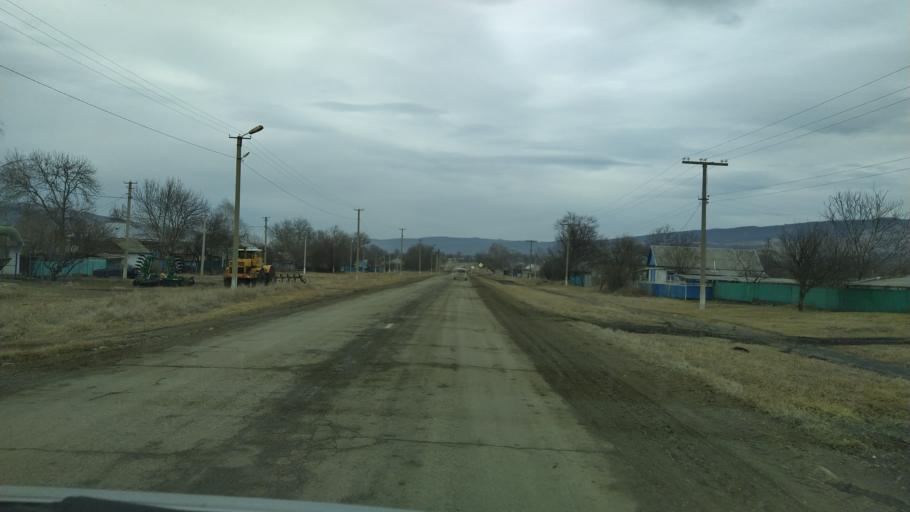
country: RU
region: Krasnodarskiy
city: Peredovaya
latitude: 44.1144
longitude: 41.4569
